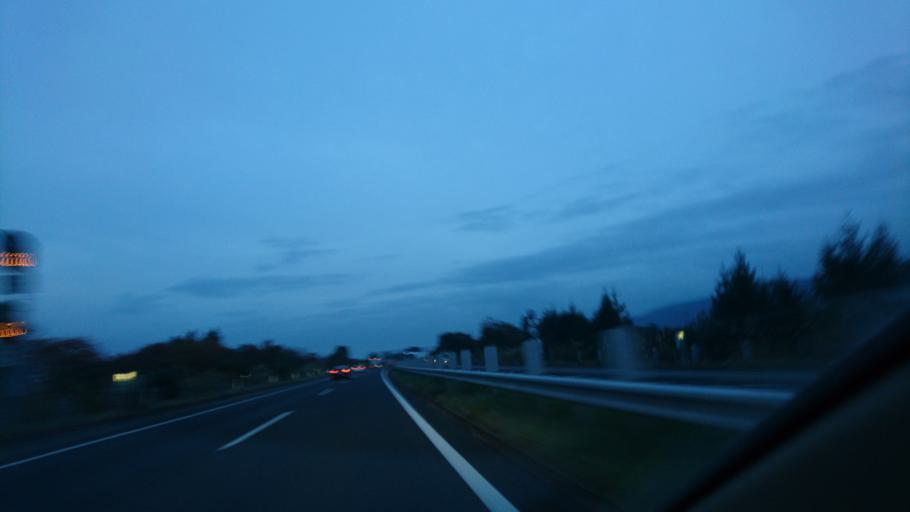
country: JP
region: Iwate
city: Morioka-shi
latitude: 39.5736
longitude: 141.1208
